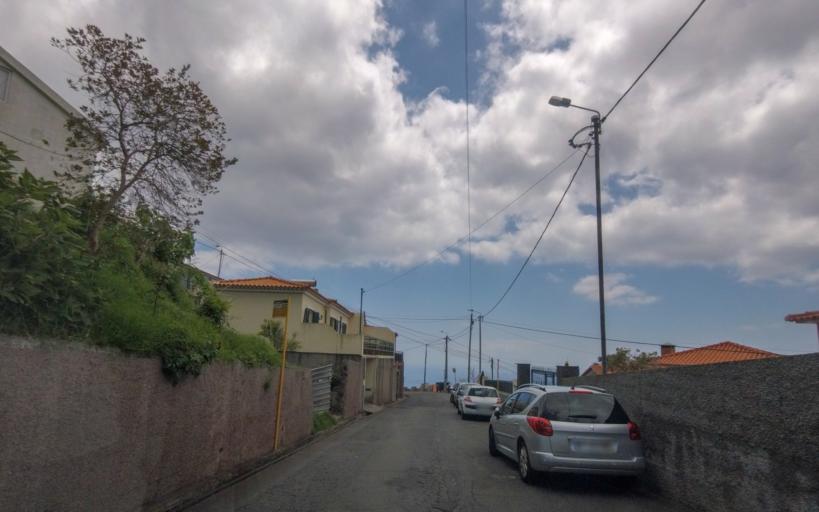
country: PT
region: Madeira
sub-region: Funchal
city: Nossa Senhora do Monte
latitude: 32.6662
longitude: -16.8801
